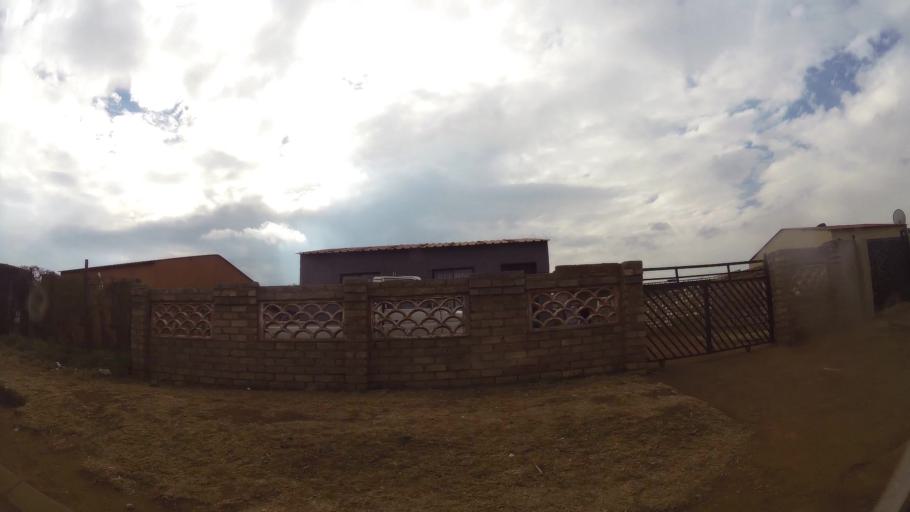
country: ZA
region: Gauteng
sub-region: Ekurhuleni Metropolitan Municipality
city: Germiston
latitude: -26.4010
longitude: 28.1520
